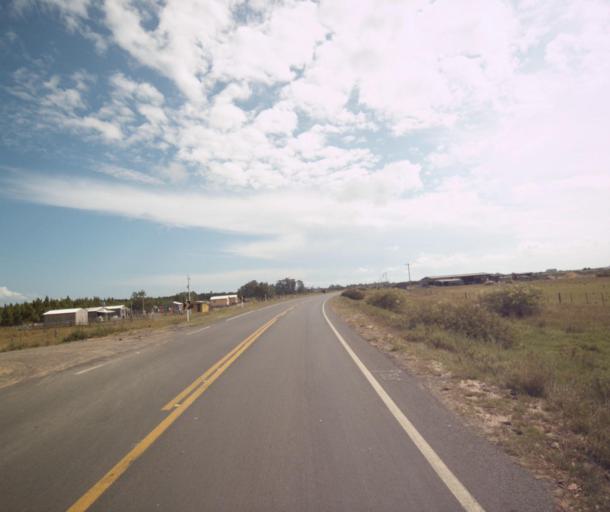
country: BR
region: Rio Grande do Sul
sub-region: Sao Lourenco Do Sul
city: Sao Lourenco do Sul
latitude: -31.6076
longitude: -51.3879
